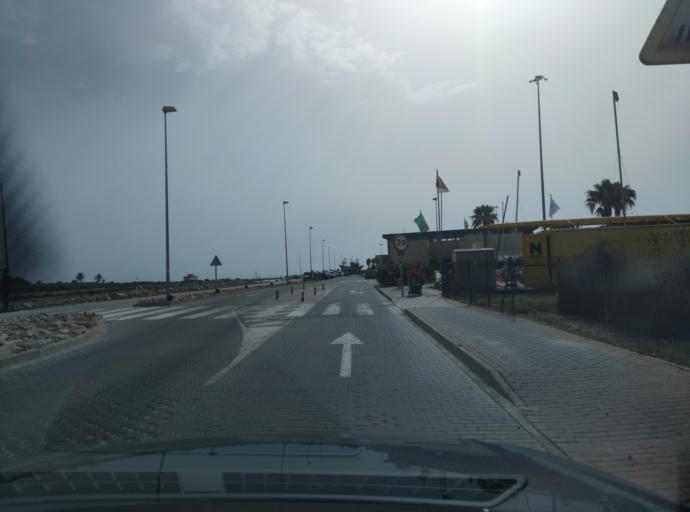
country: ES
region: Valencia
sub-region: Provincia de Alicante
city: Guardamar del Segura
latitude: 38.1097
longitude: -0.6475
